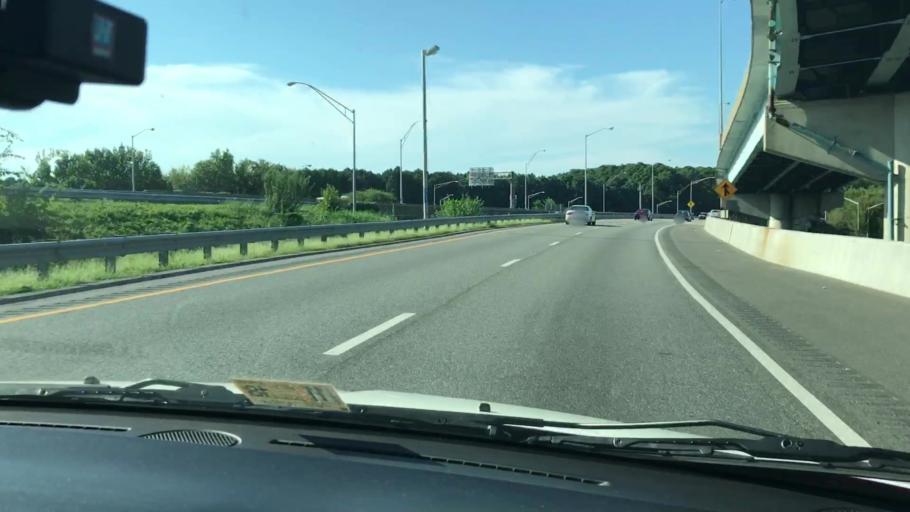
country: US
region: Virginia
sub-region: City of Norfolk
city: Norfolk
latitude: 36.9200
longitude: -76.2699
